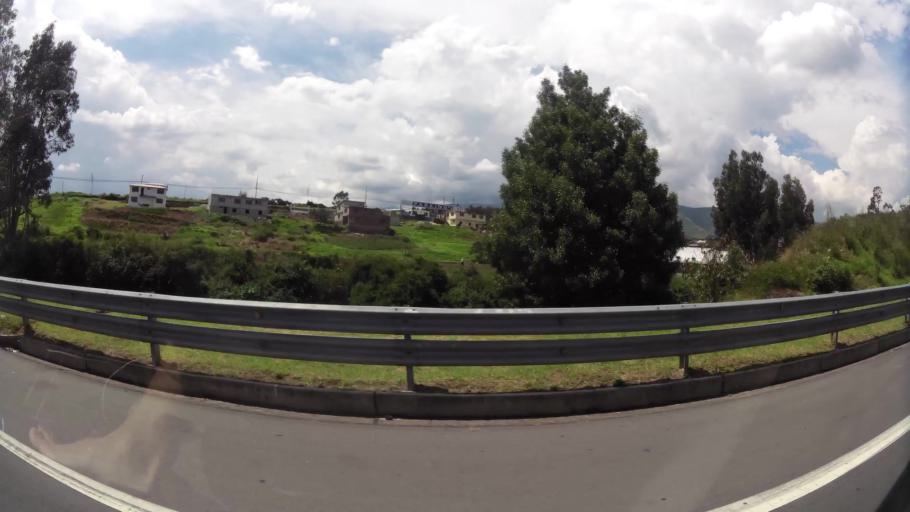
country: EC
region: Pichincha
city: Sangolqui
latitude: -0.1874
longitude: -78.3392
